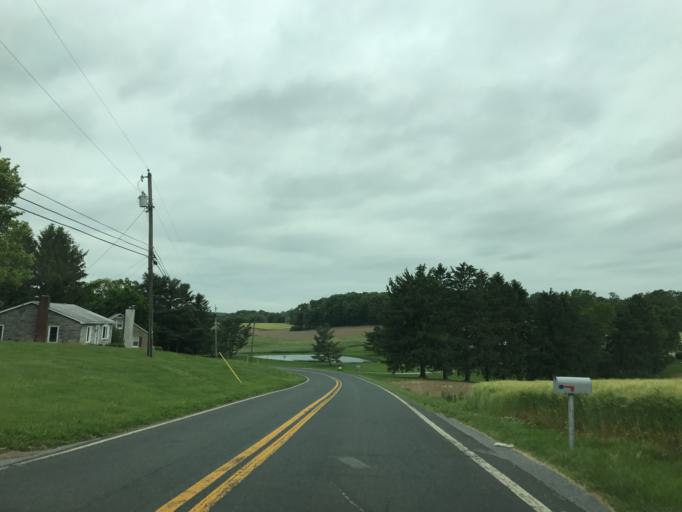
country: US
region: Maryland
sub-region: Carroll County
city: Hampstead
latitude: 39.6362
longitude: -76.8429
